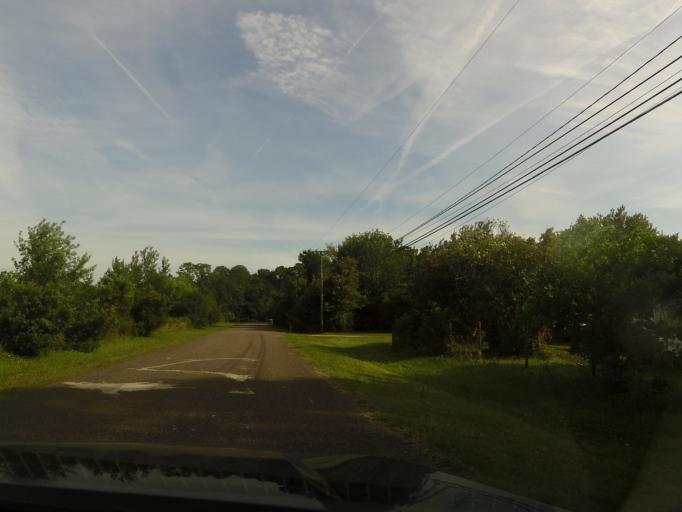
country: US
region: Florida
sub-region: Nassau County
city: Fernandina Beach
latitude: 30.5281
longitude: -81.4871
